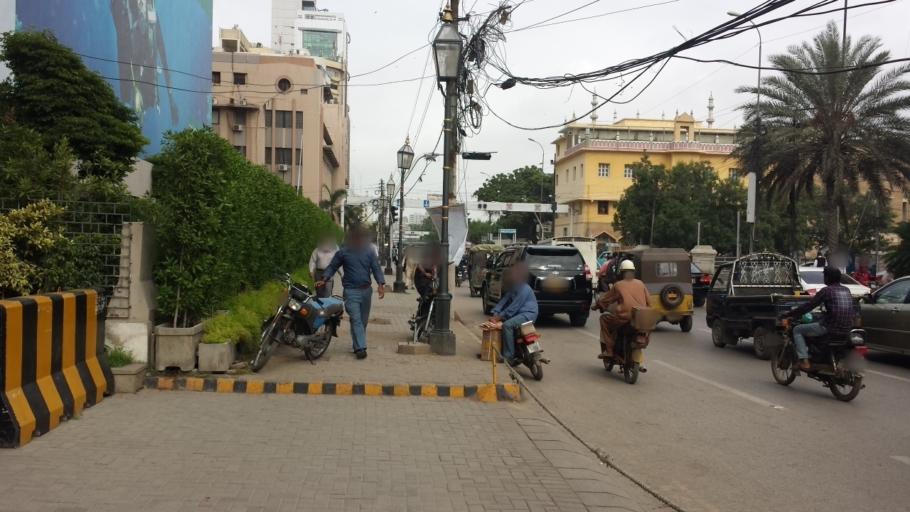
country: PK
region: Sindh
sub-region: Karachi District
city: Karachi
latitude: 24.8496
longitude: 67.0050
